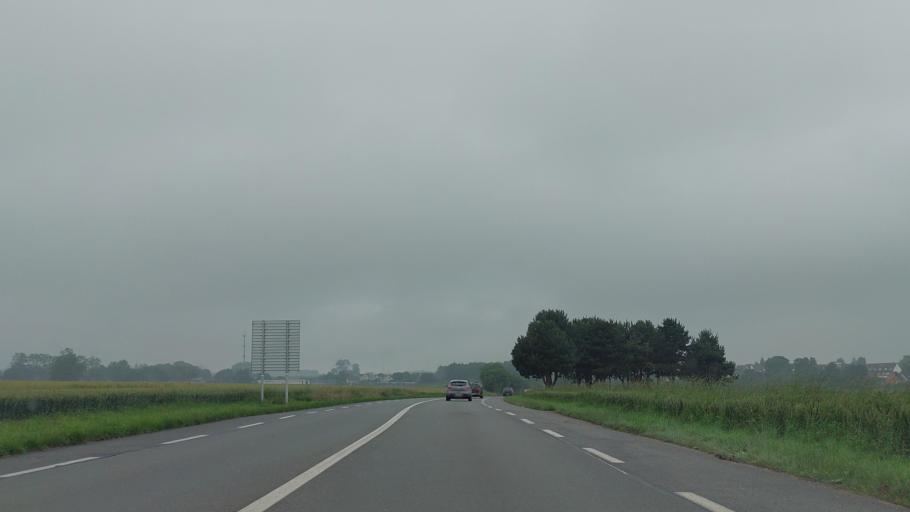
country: FR
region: Picardie
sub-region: Departement de la Somme
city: Friville-Escarbotin
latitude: 50.0733
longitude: 1.5559
